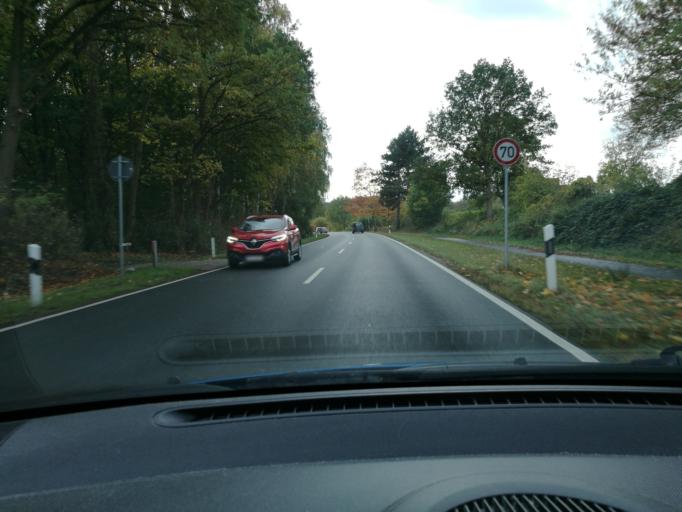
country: DE
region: Schleswig-Holstein
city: Gross Sarau
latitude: 53.7616
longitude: 10.7304
